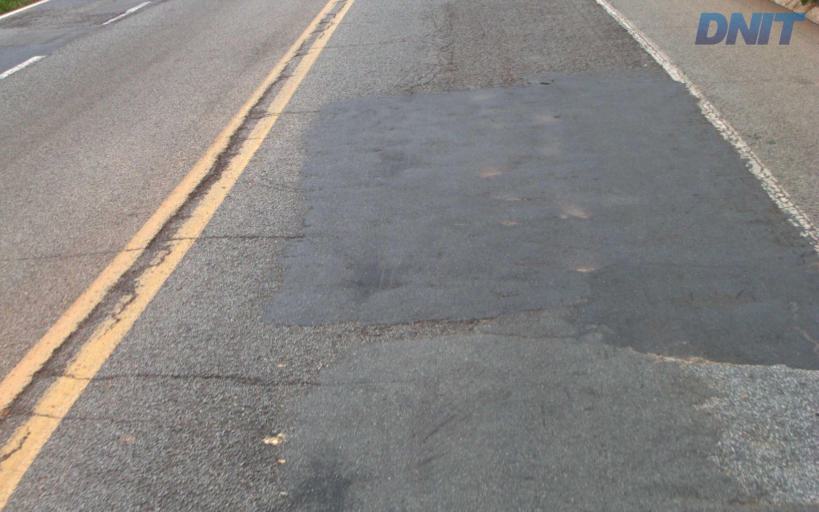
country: BR
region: Minas Gerais
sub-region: Barao De Cocais
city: Barao de Cocais
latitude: -19.8298
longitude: -43.3809
